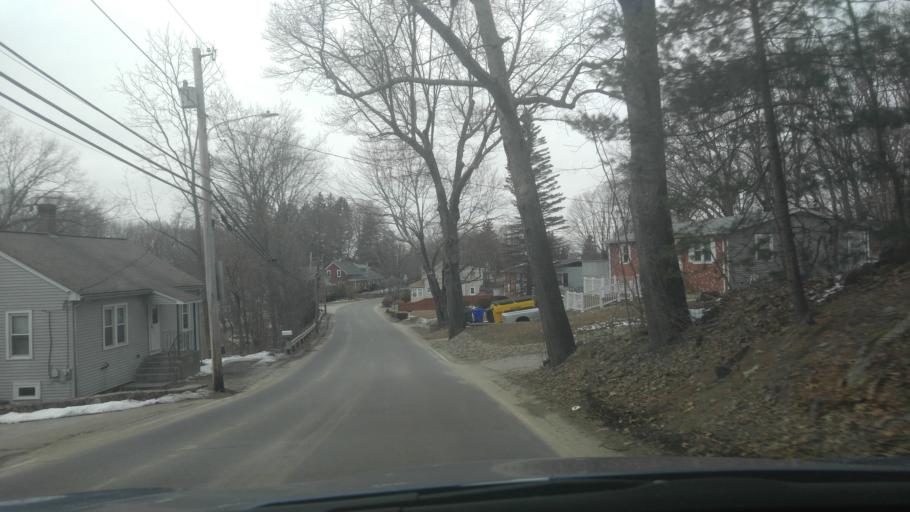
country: US
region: Rhode Island
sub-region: Kent County
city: West Warwick
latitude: 41.6791
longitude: -71.5221
